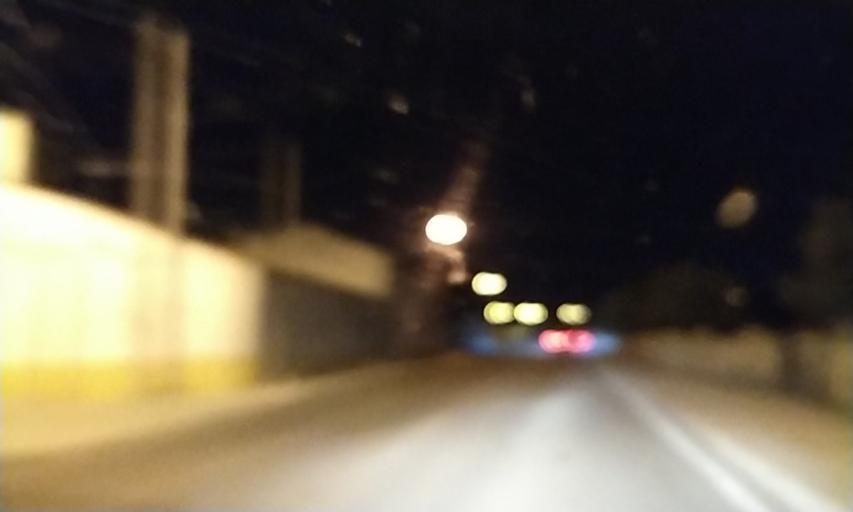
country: PT
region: Evora
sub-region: Estremoz
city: Estremoz
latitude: 38.8457
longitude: -7.5961
